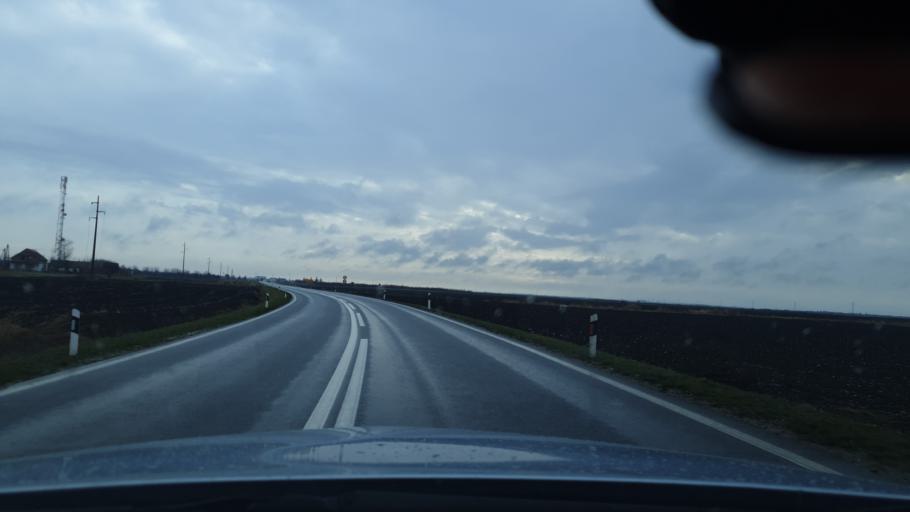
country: RS
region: Autonomna Pokrajina Vojvodina
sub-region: Juznobanatski Okrug
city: Kovin
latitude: 44.8101
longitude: 20.8602
